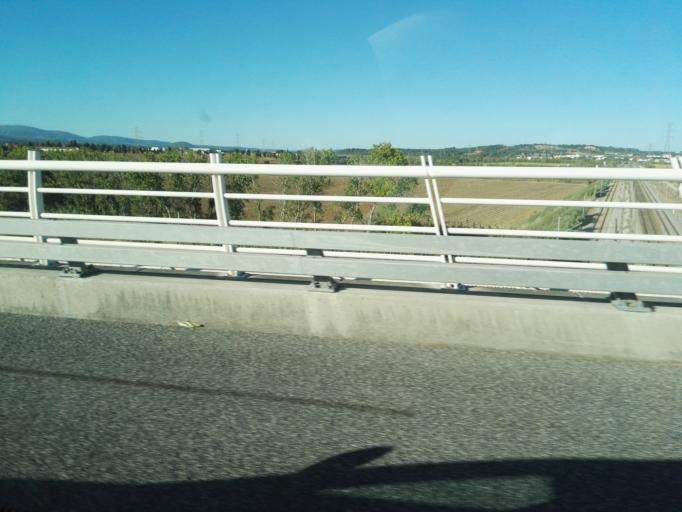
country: PT
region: Lisbon
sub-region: Alenquer
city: Carregado
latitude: 39.0160
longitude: -8.9465
